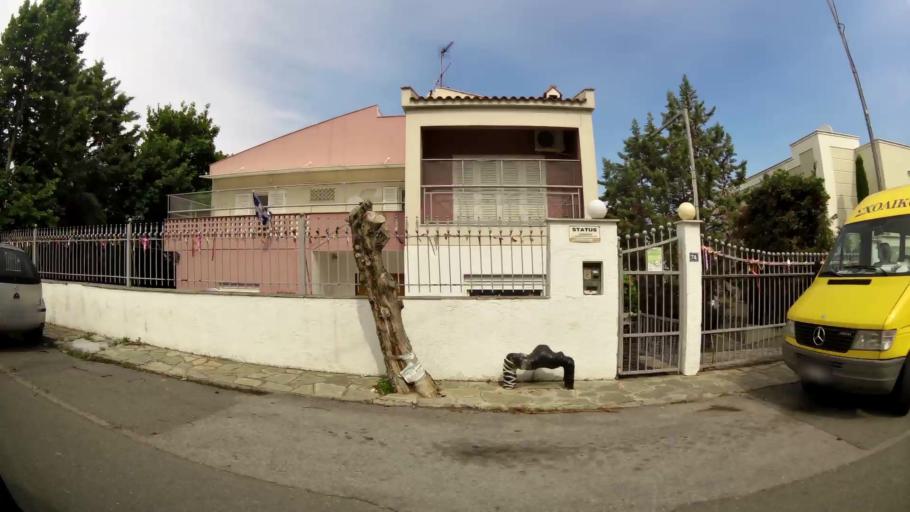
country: GR
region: Central Macedonia
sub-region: Nomos Thessalonikis
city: Panorama
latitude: 40.5800
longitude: 23.0263
